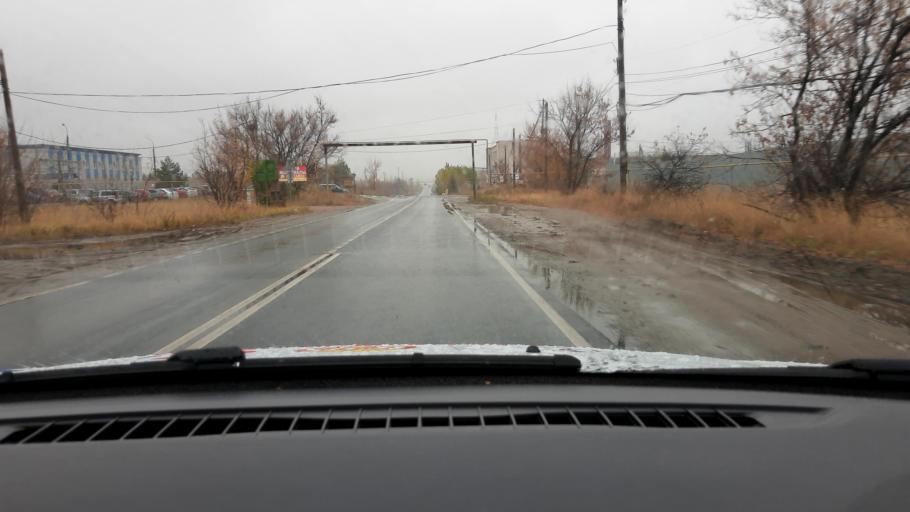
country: RU
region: Nizjnij Novgorod
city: Babino
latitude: 56.2593
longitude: 43.5937
